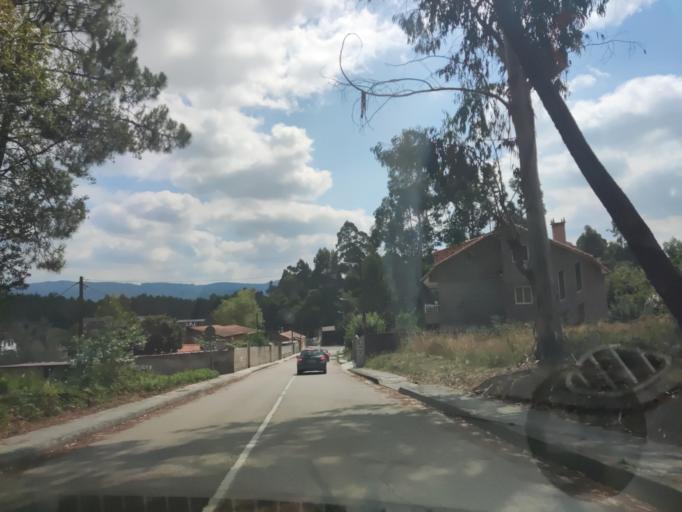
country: ES
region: Galicia
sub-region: Provincia de Pontevedra
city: Porrino
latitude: 42.1462
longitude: -8.6468
